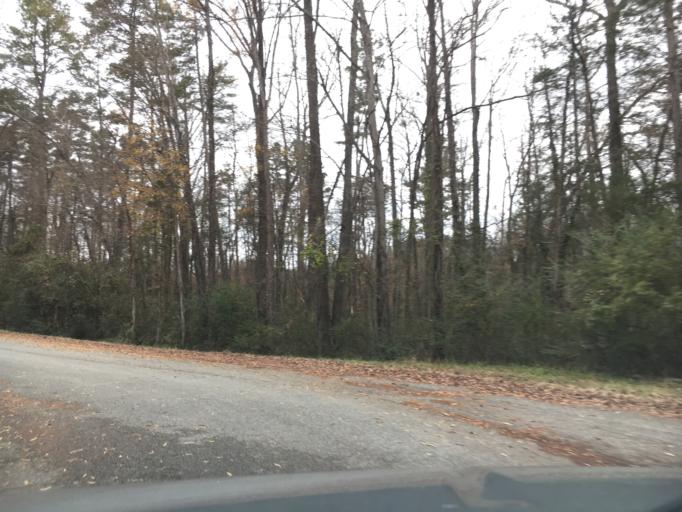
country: US
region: Virginia
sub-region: Halifax County
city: South Boston
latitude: 36.7102
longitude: -78.8924
